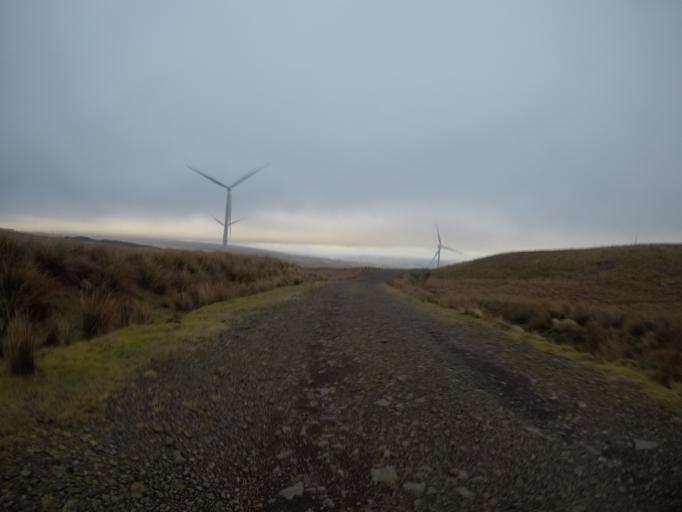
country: GB
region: Scotland
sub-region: North Ayrshire
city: Dalry
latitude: 55.7384
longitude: -4.7804
